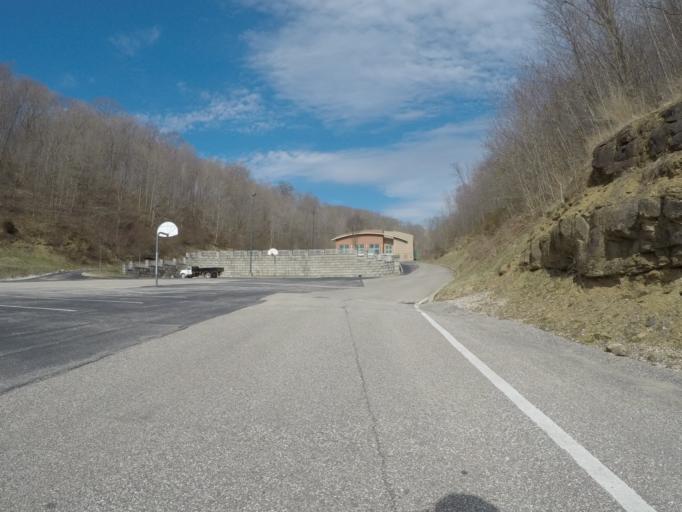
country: US
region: West Virginia
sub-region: Cabell County
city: Huntington
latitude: 38.3991
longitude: -82.4560
